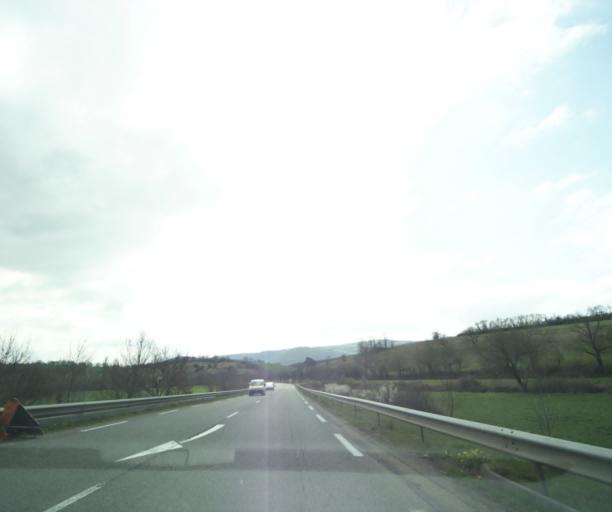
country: FR
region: Midi-Pyrenees
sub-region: Departement de l'Aveyron
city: Laissac
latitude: 44.3565
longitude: 2.9071
